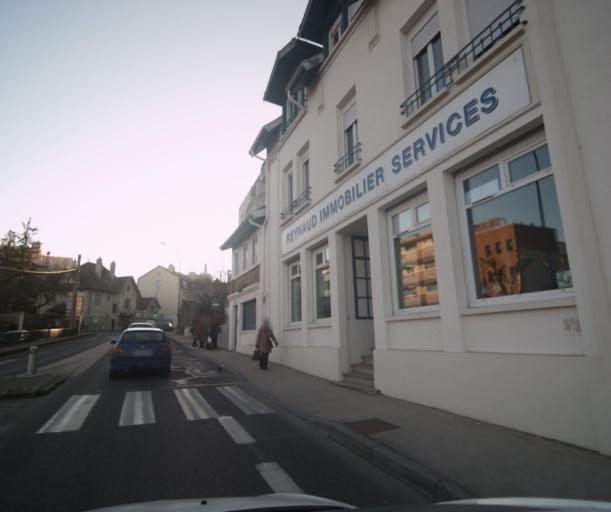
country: FR
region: Franche-Comte
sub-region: Departement du Doubs
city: Besancon
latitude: 47.2396
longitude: 6.0132
